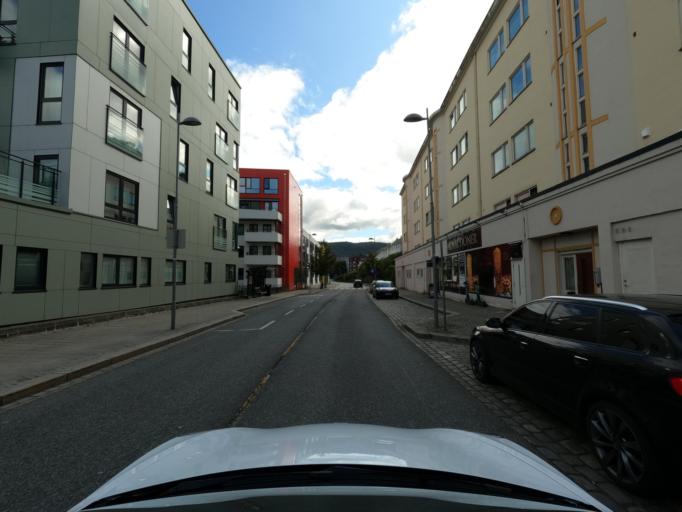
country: NO
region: Hordaland
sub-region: Bergen
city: Bergen
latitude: 60.3782
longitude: 5.3270
